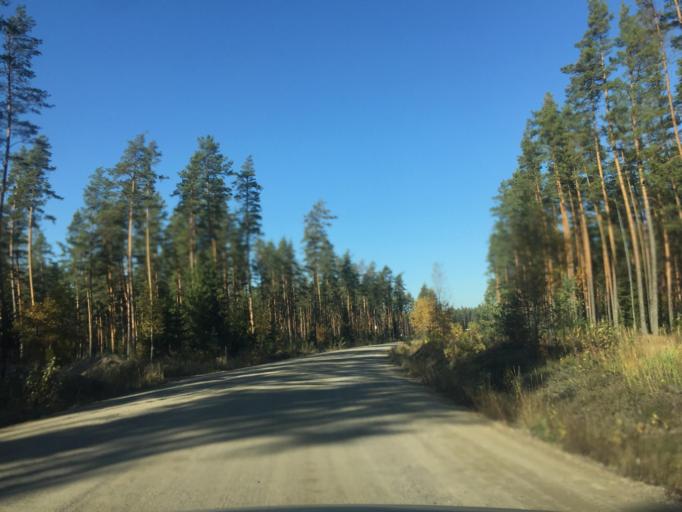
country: RU
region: Republic of Karelia
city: Lakhdenpokh'ya
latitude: 61.3836
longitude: 29.9644
